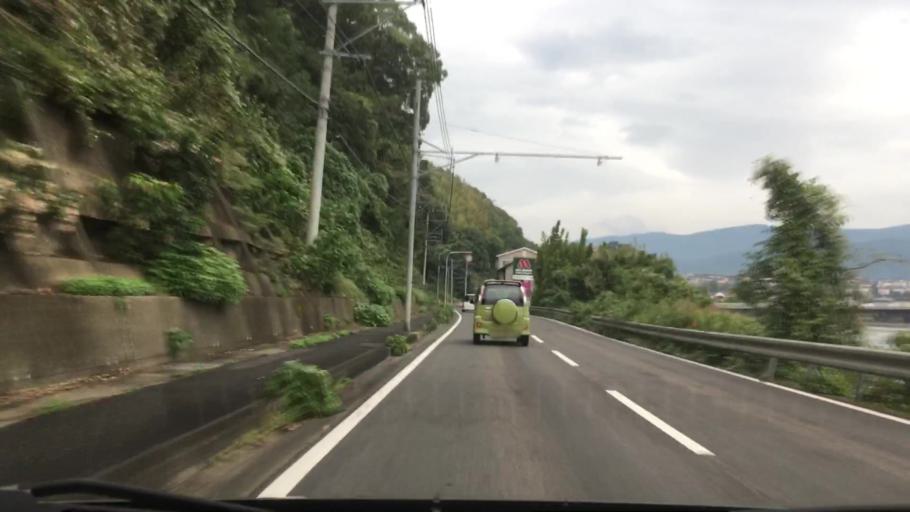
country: JP
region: Nagasaki
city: Sasebo
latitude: 33.1238
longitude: 129.7931
